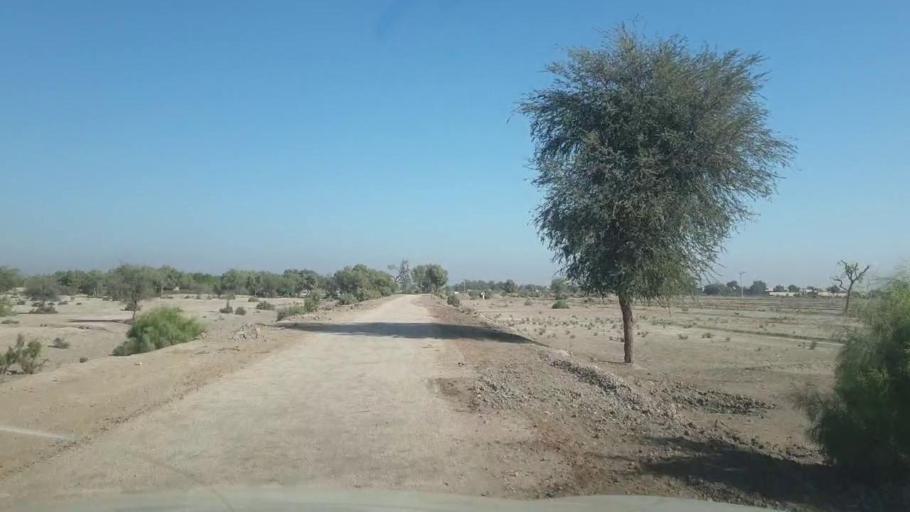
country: PK
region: Sindh
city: Bhan
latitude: 26.5449
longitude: 67.6545
